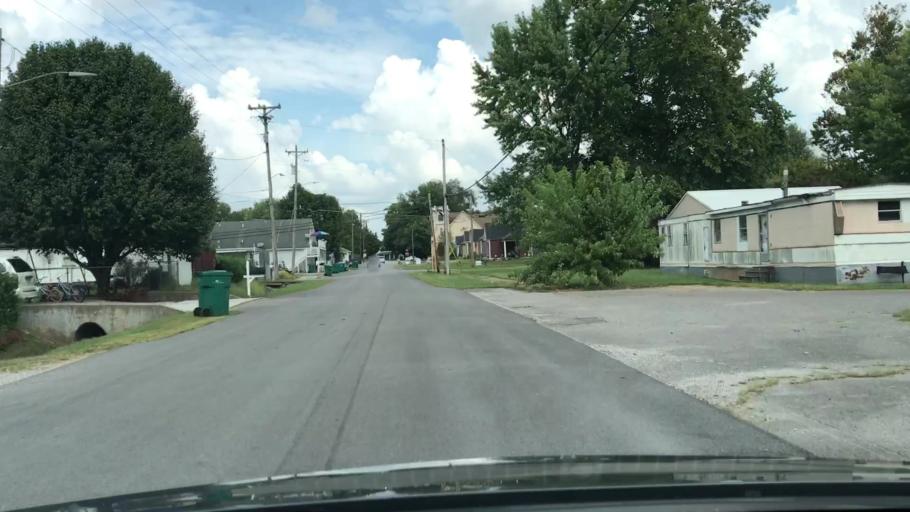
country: US
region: Kentucky
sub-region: Todd County
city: Elkton
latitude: 36.8072
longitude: -87.1507
